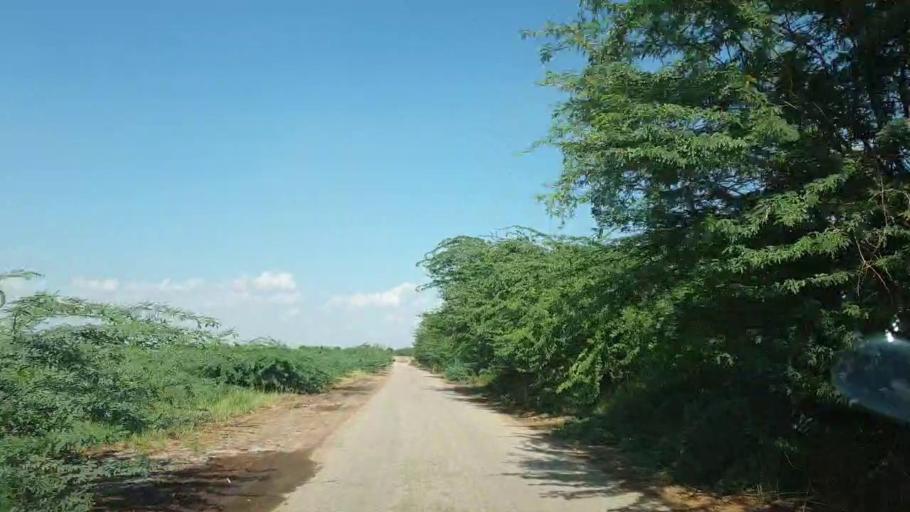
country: PK
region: Sindh
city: Pithoro
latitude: 25.6256
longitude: 69.4299
